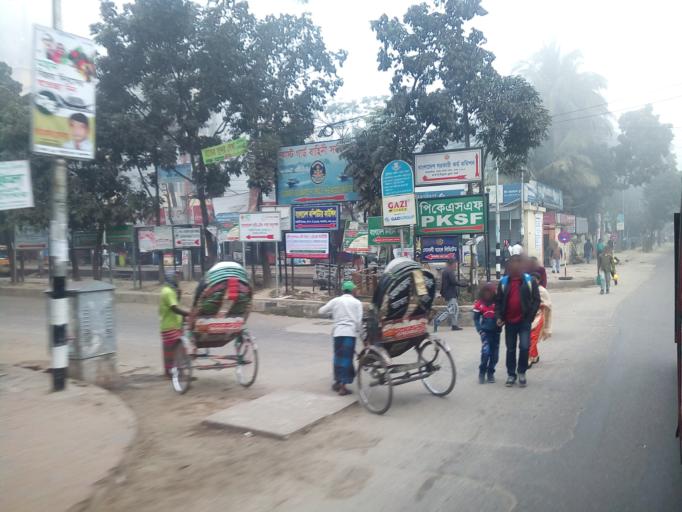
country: BD
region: Dhaka
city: Azimpur
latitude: 23.7790
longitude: 90.3798
